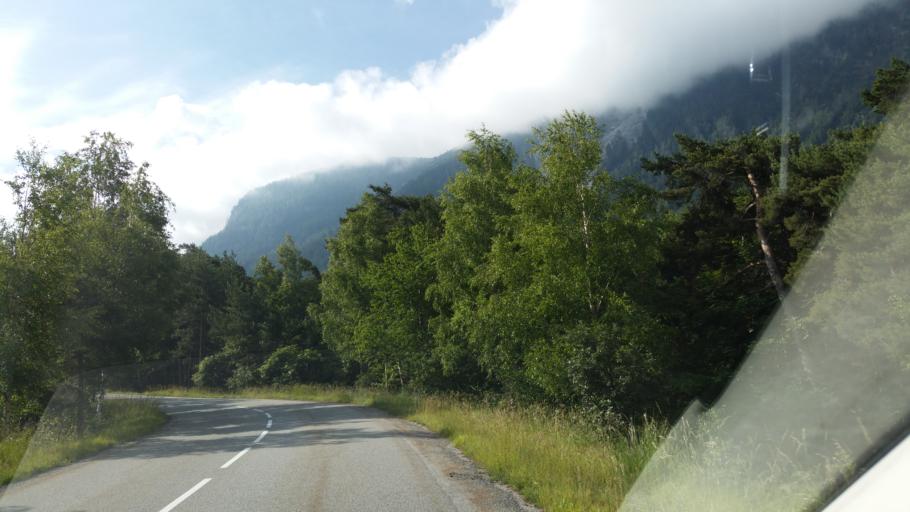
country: FR
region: Rhone-Alpes
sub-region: Departement de la Savoie
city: Modane
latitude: 45.2023
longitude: 6.6084
